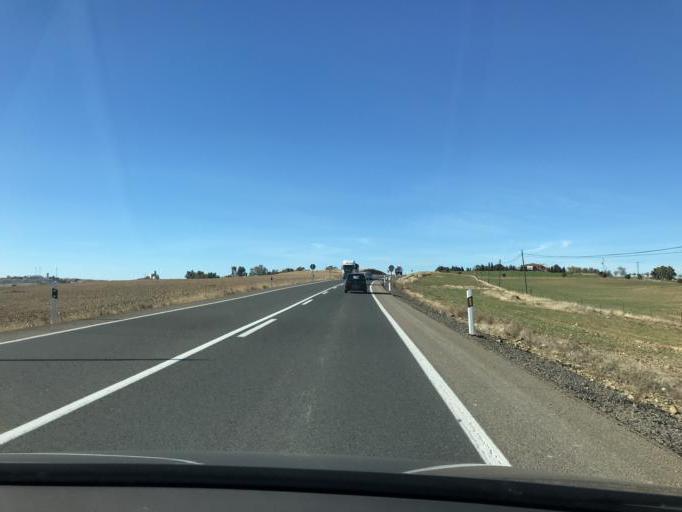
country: ES
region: Extremadura
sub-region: Provincia de Badajoz
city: Azuaga
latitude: 38.2769
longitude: -5.6667
